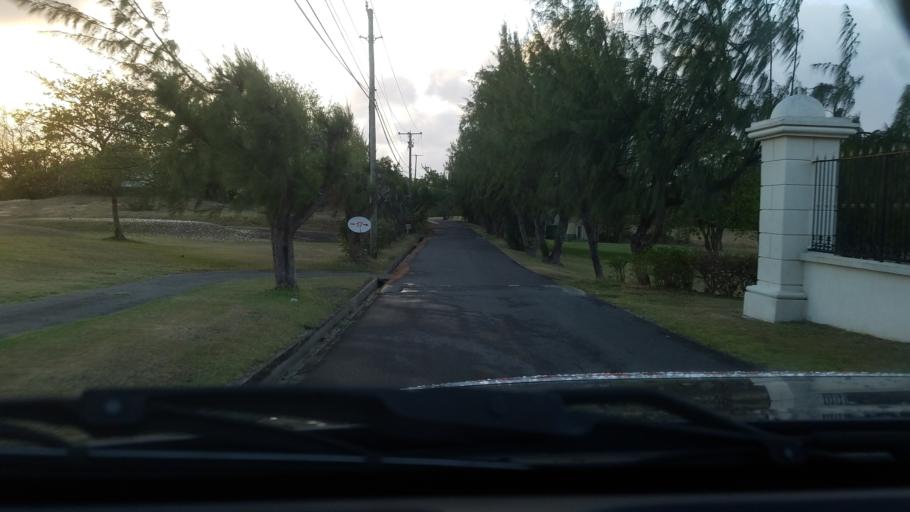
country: LC
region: Gros-Islet
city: Gros Islet
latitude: 14.0950
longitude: -60.9430
